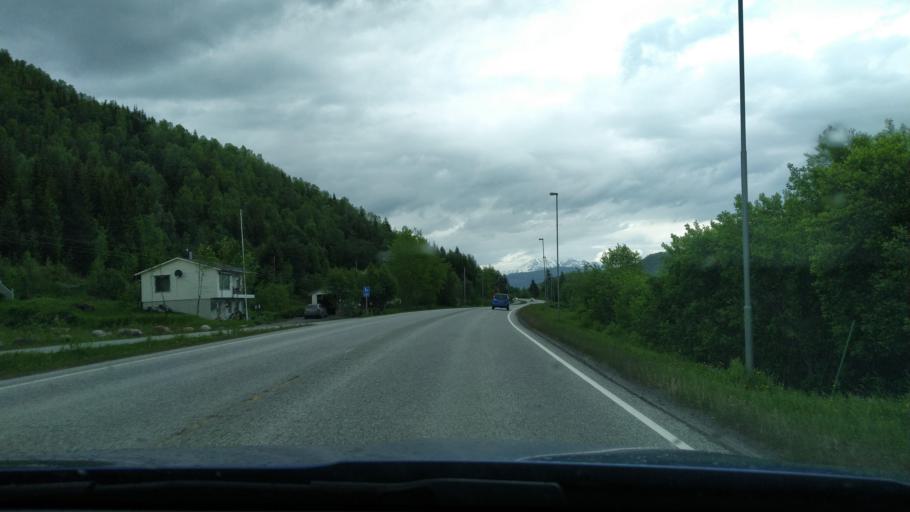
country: NO
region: Troms
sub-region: Malselv
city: Moen
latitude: 69.0227
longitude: 18.4915
